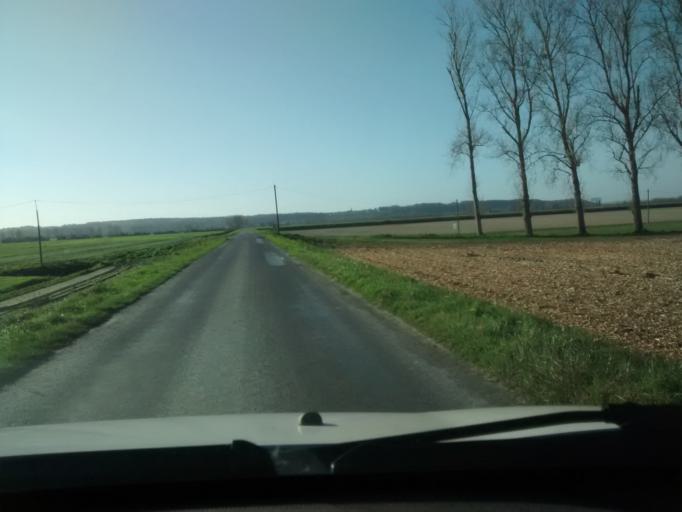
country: FR
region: Brittany
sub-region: Departement d'Ille-et-Vilaine
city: Roz-sur-Couesnon
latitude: 48.6117
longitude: -1.5517
